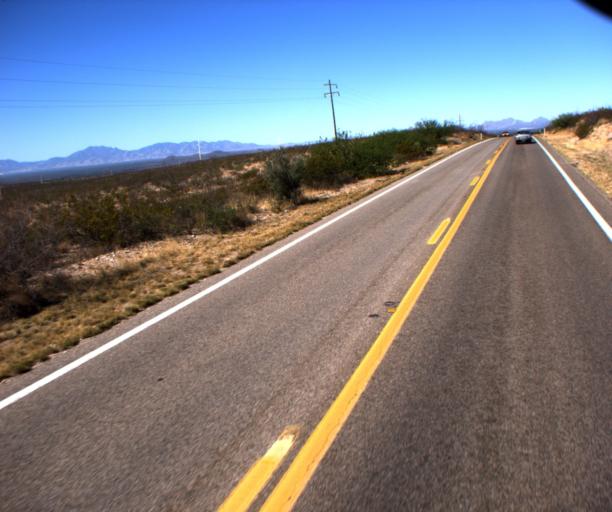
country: US
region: Arizona
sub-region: Cochise County
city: Tombstone
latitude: 31.7439
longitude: -110.1365
